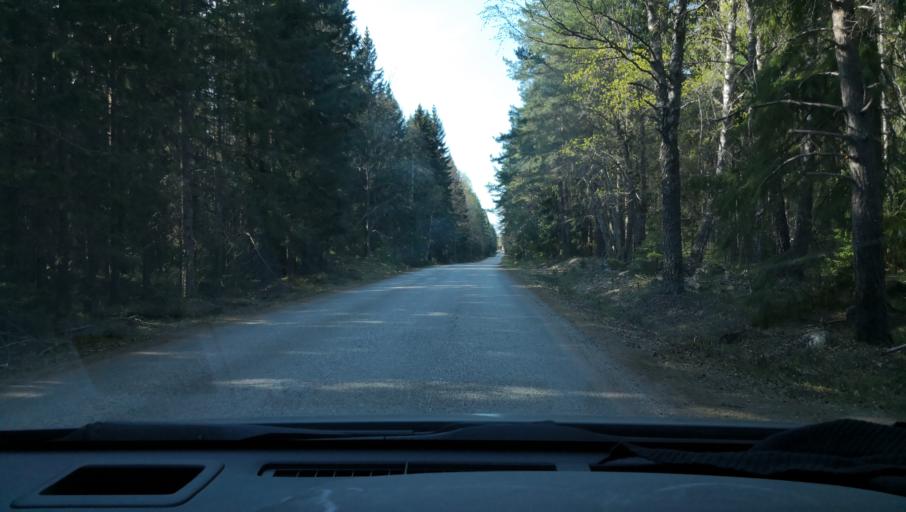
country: SE
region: Uppsala
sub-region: Heby Kommun
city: Tarnsjo
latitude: 60.2774
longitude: 16.8935
